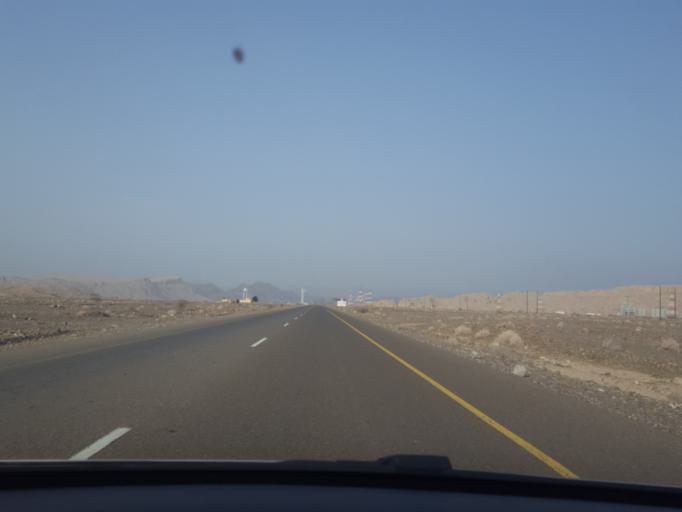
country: AE
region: Abu Dhabi
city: Al Ain
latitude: 24.0336
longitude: 56.0034
